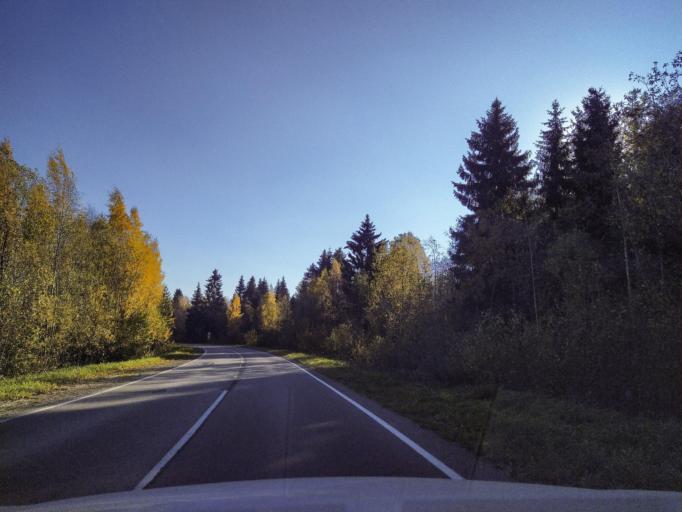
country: RU
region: Leningrad
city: Siverskiy
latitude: 59.3095
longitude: 30.0292
